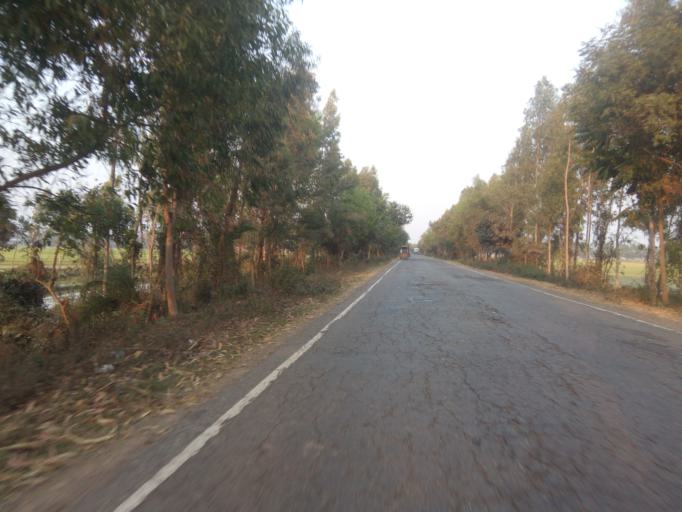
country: BD
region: Rajshahi
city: Bogra
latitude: 24.5675
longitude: 89.2108
